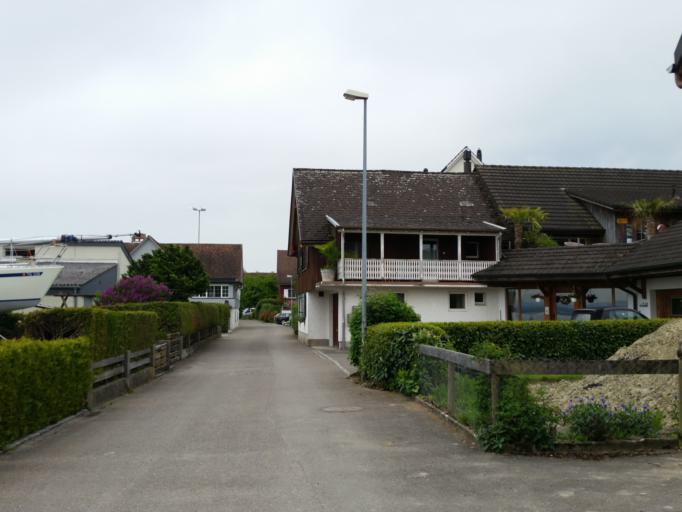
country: CH
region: Thurgau
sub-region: Arbon District
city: Uttwil
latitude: 47.5975
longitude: 9.3191
